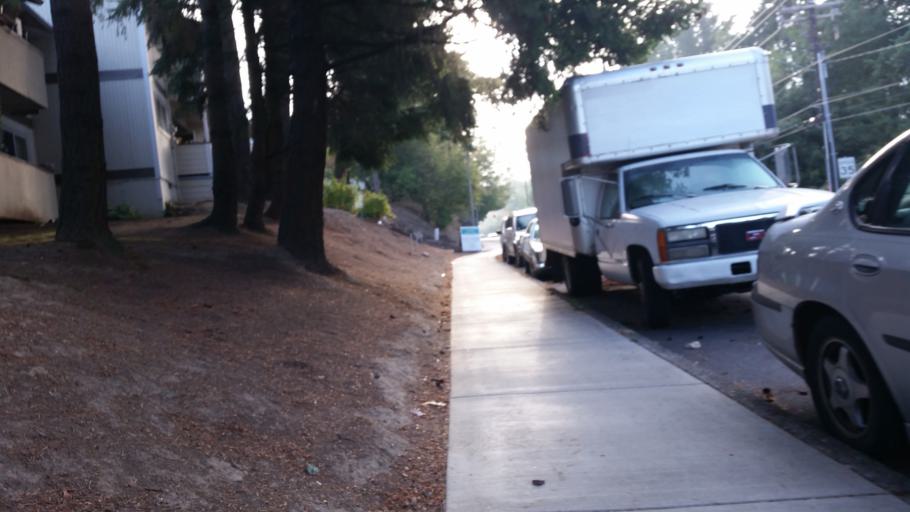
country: US
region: Oregon
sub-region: Washington County
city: Garden Home-Whitford
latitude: 45.4670
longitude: -122.7113
